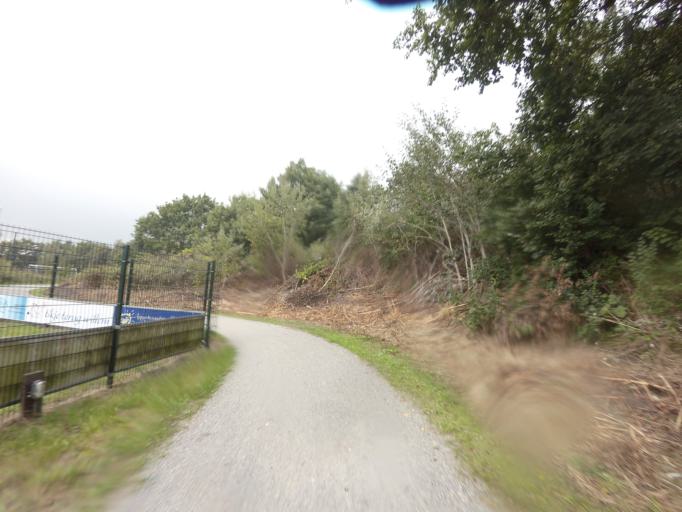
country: NL
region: Friesland
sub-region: Gemeente Schiermonnikoog
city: Schiermonnikoog
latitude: 53.4831
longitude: 6.1640
